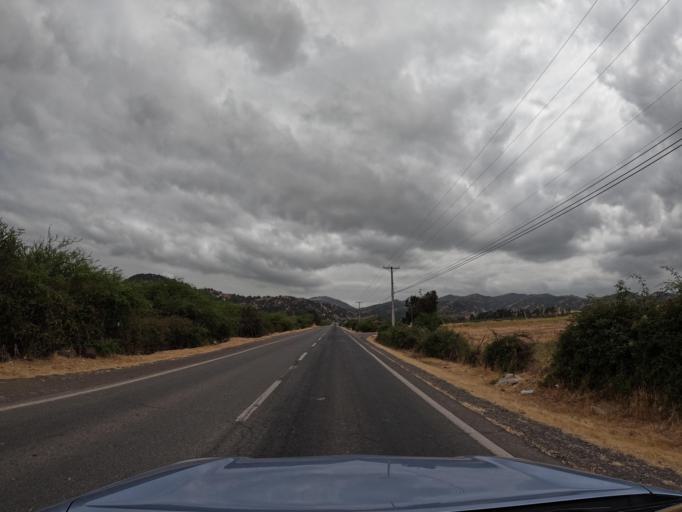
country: CL
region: Maule
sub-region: Provincia de Curico
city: Teno
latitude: -34.8359
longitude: -71.1886
